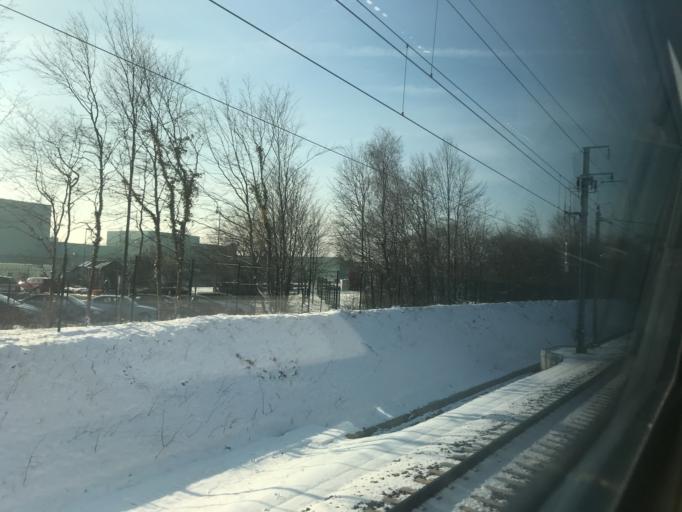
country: LU
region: Luxembourg
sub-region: Canton de Luxembourg
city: Sandweiler
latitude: 49.6002
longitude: 6.2063
